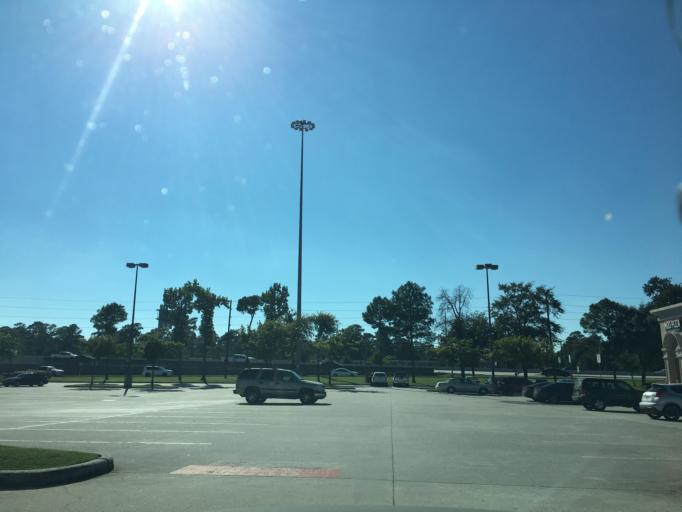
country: US
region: Texas
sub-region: Montgomery County
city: Shenandoah
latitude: 30.1824
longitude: -95.4508
